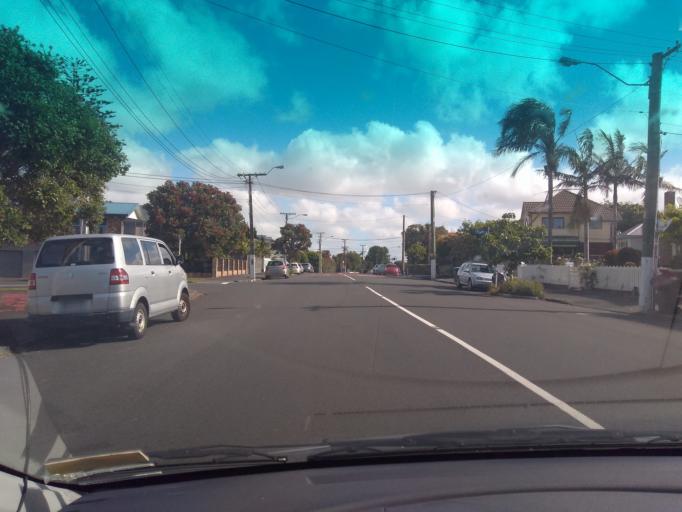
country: NZ
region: Auckland
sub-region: Auckland
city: Rosebank
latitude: -36.8535
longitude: 174.7041
